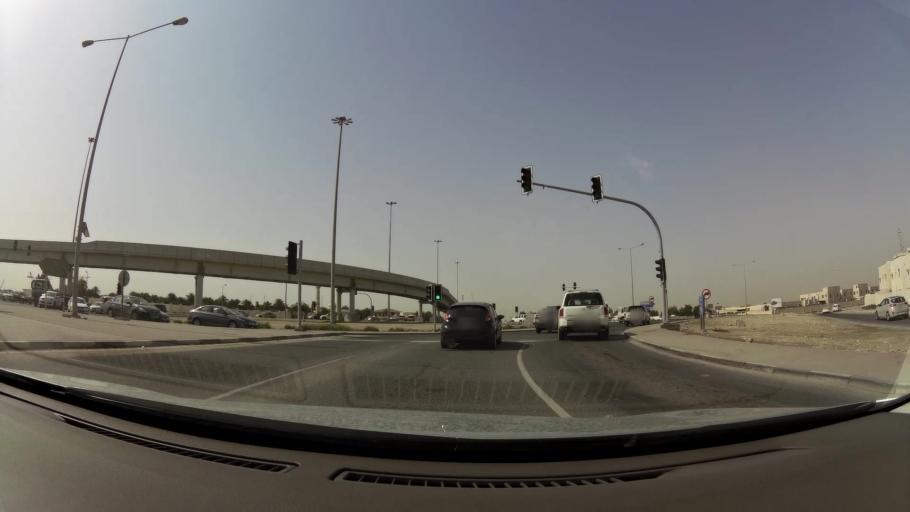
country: QA
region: Baladiyat ad Dawhah
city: Doha
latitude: 25.2382
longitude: 51.5230
